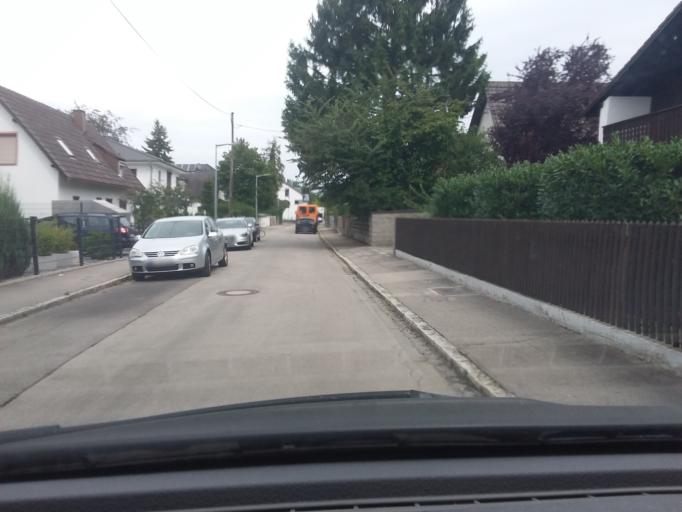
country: DE
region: Bavaria
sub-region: Upper Bavaria
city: Oberschleissheim
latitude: 48.2120
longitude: 11.5443
